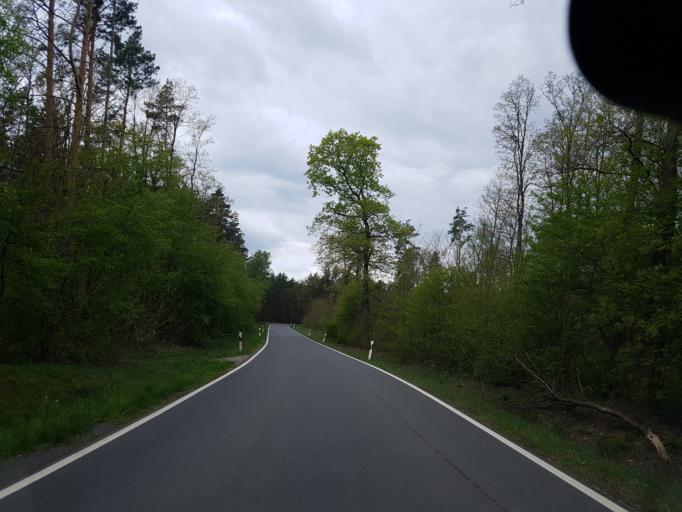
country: DE
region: Brandenburg
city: Bronkow
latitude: 51.6413
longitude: 13.9677
